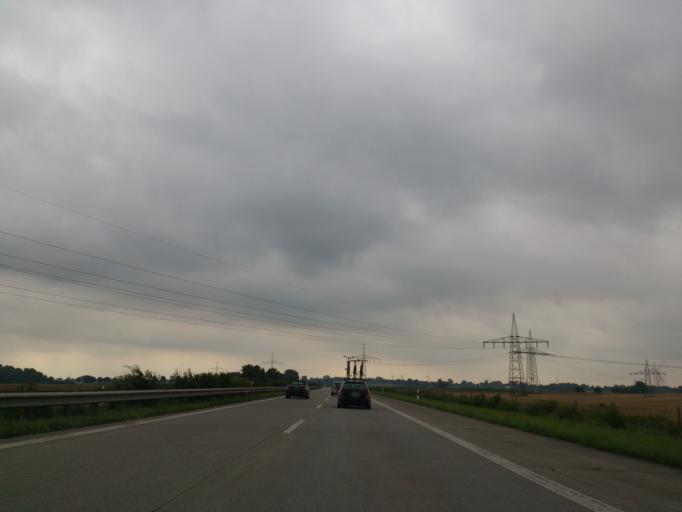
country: DE
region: Schleswig-Holstein
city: Neuenbrook
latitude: 53.8585
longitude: 9.5748
